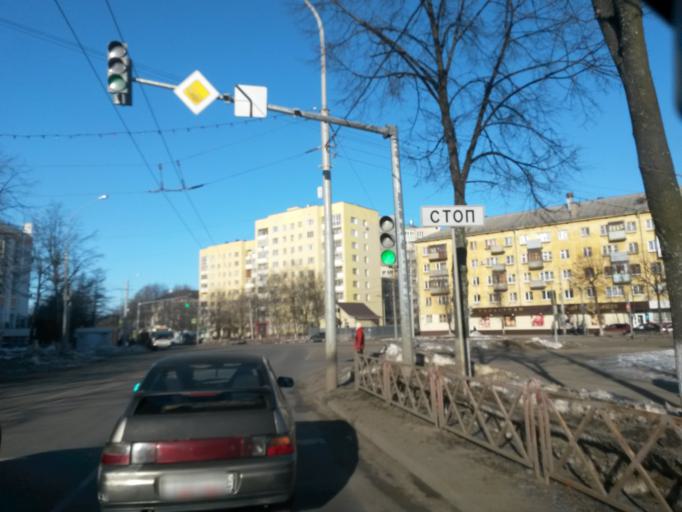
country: RU
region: Jaroslavl
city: Yaroslavl
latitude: 57.6270
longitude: 39.8454
